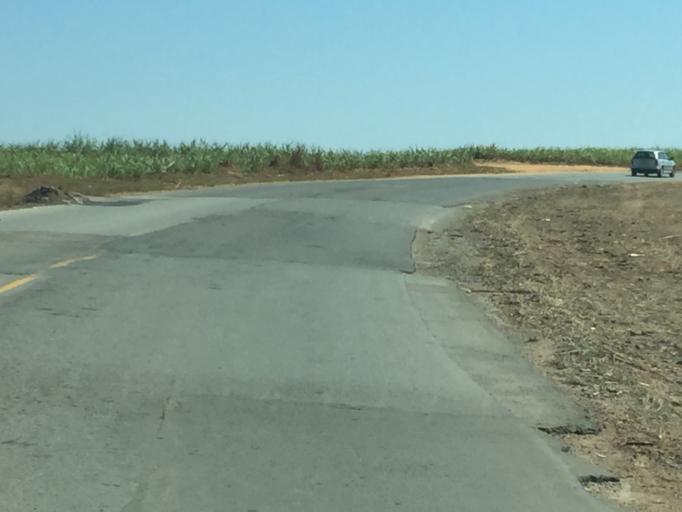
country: BR
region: Sao Paulo
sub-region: Itapira
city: Itapira
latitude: -22.3978
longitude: -46.8570
